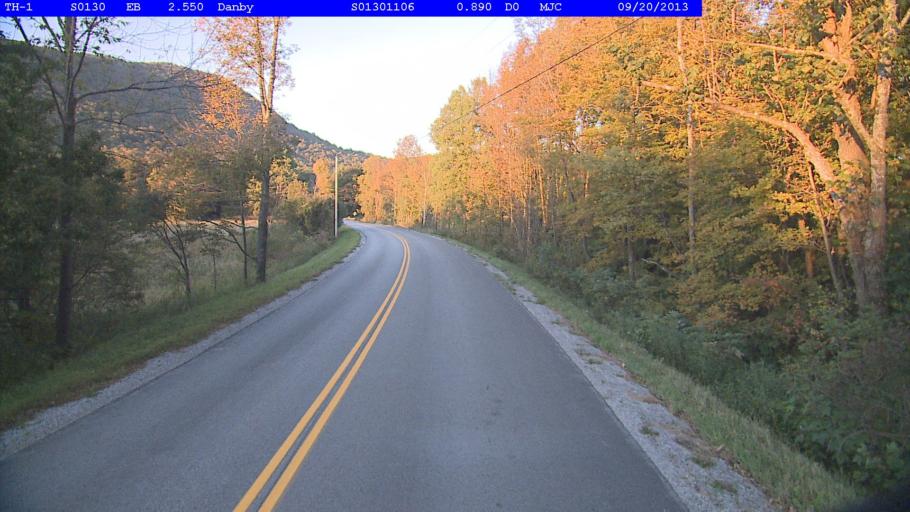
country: US
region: New York
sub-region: Washington County
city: Granville
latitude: 43.3645
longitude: -73.1062
